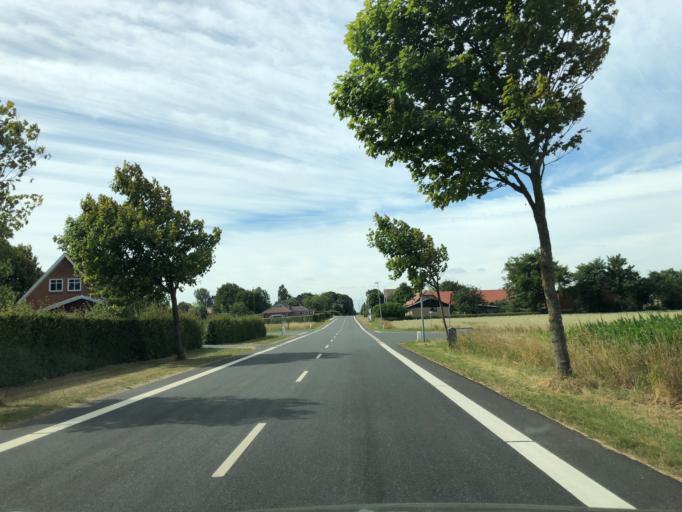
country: DK
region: Central Jutland
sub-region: Viborg Kommune
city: Viborg
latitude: 56.5380
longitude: 9.4706
